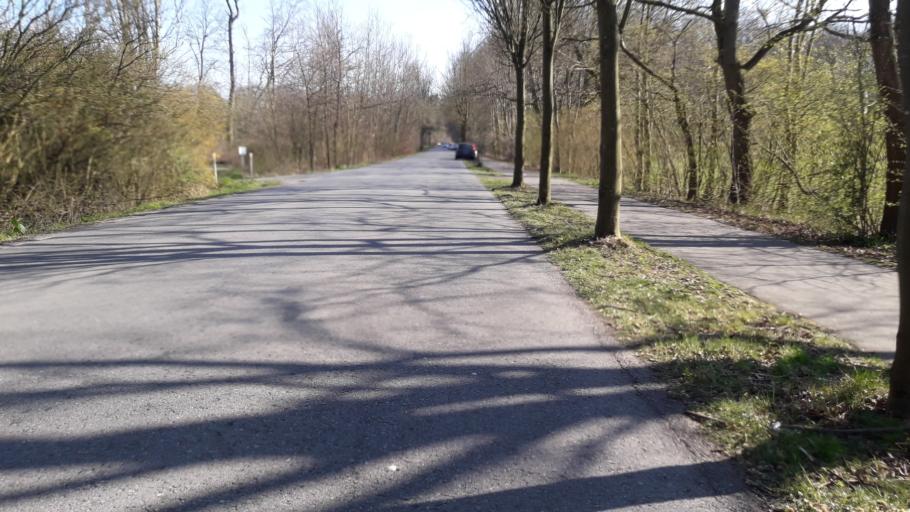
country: DE
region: North Rhine-Westphalia
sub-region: Regierungsbezirk Detmold
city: Paderborn
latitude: 51.6809
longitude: 8.6869
